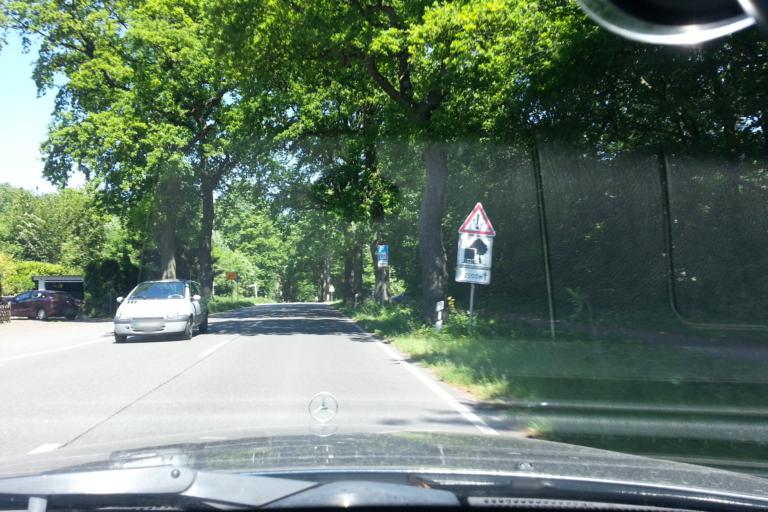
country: DE
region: North Rhine-Westphalia
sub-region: Regierungsbezirk Munster
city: Recklinghausen
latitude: 51.6723
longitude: 7.1801
